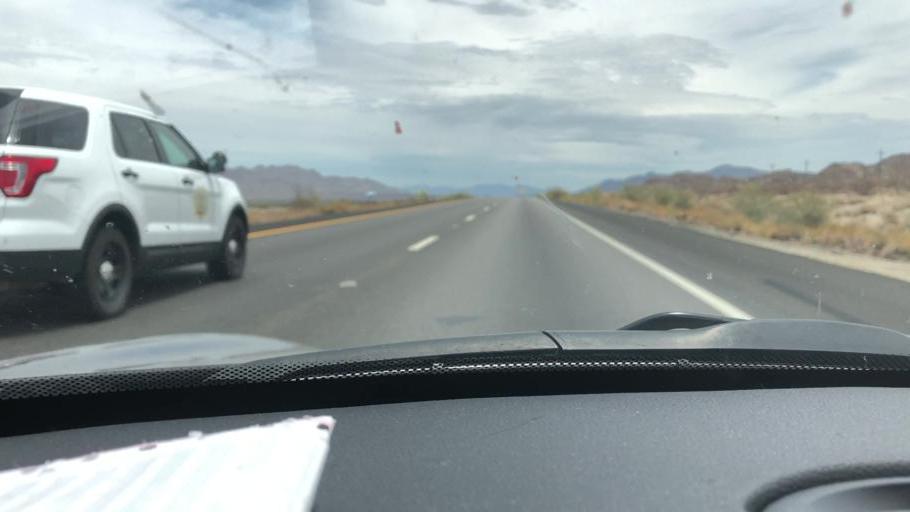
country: US
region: California
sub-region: Riverside County
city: Mecca
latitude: 33.6625
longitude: -115.7051
